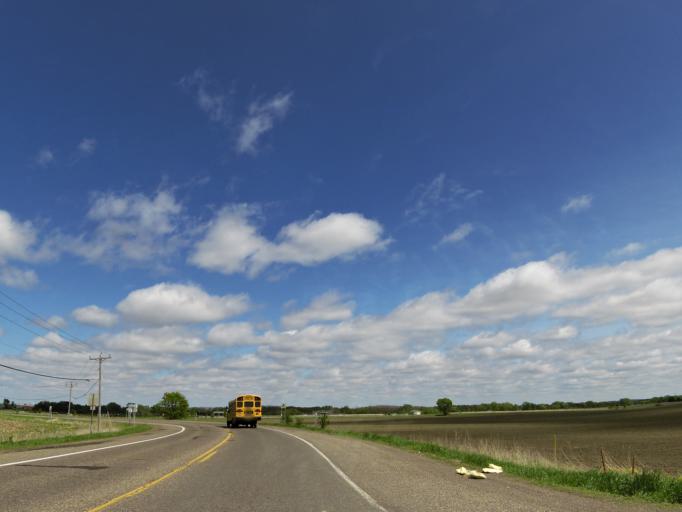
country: US
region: Minnesota
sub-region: Washington County
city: Lakeland
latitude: 44.9532
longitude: -92.7967
